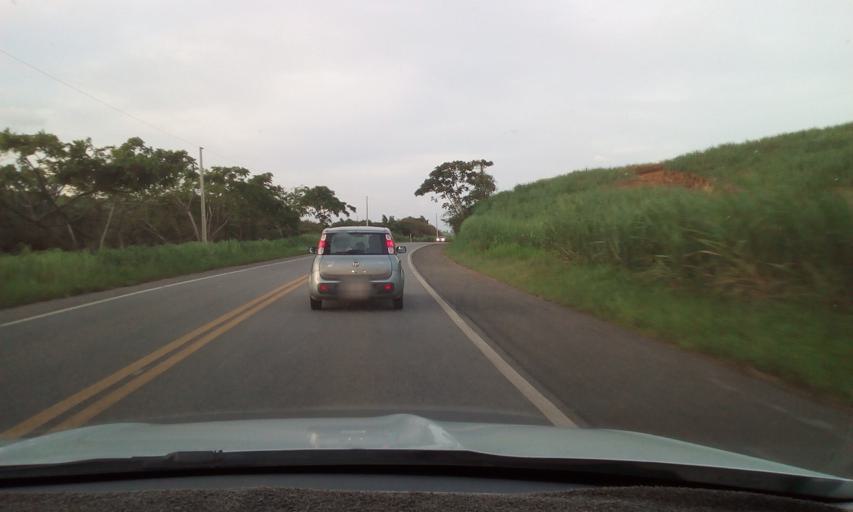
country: BR
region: Pernambuco
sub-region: Vicencia
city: Vicencia
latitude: -7.6405
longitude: -35.2545
